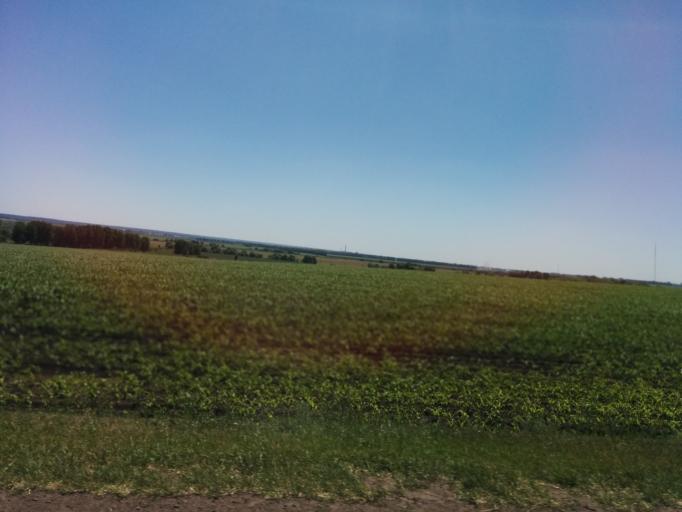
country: RU
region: Tambov
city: Donskoye
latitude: 52.8357
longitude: 41.4253
